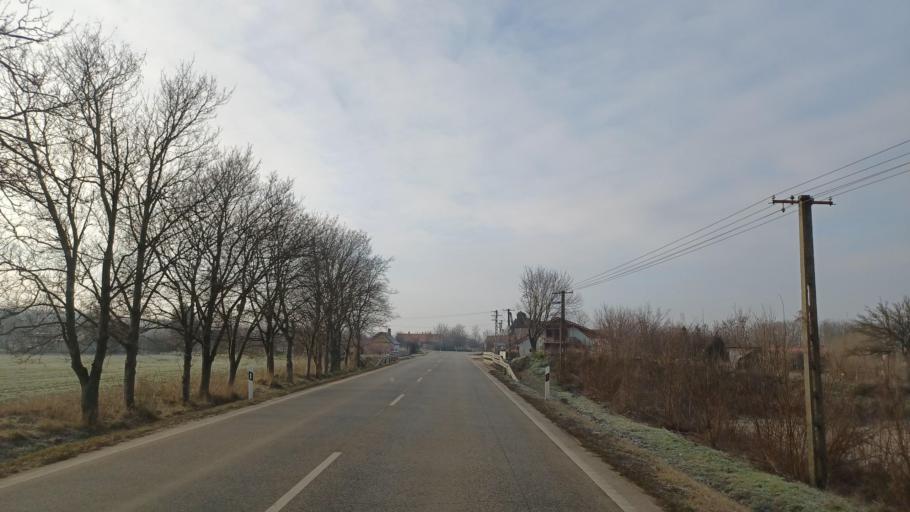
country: HU
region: Tolna
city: Simontornya
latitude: 46.7398
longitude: 18.5165
